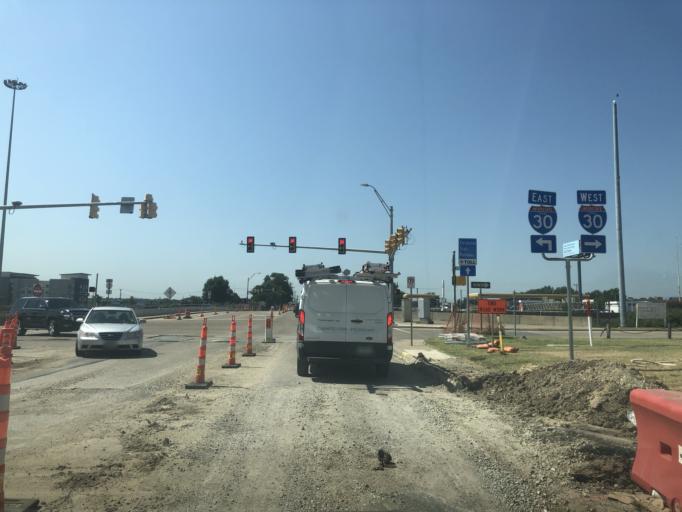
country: US
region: Texas
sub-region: Tarrant County
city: Westworth
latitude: 32.7337
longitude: -97.3701
